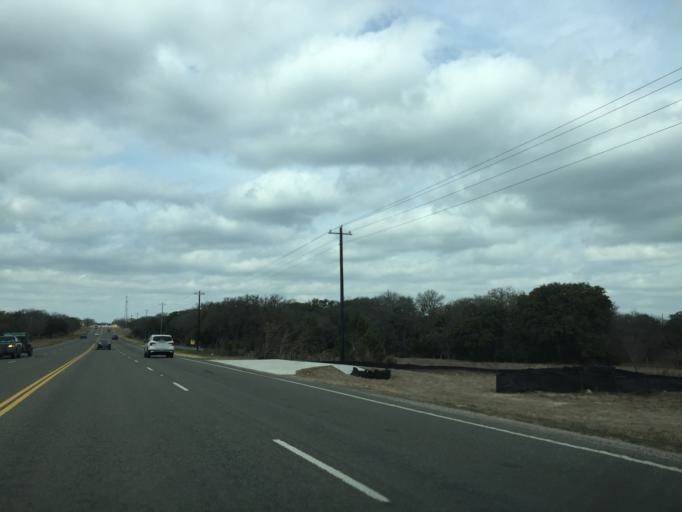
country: US
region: Texas
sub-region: Burnet County
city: Marble Falls
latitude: 30.4736
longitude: -98.1826
